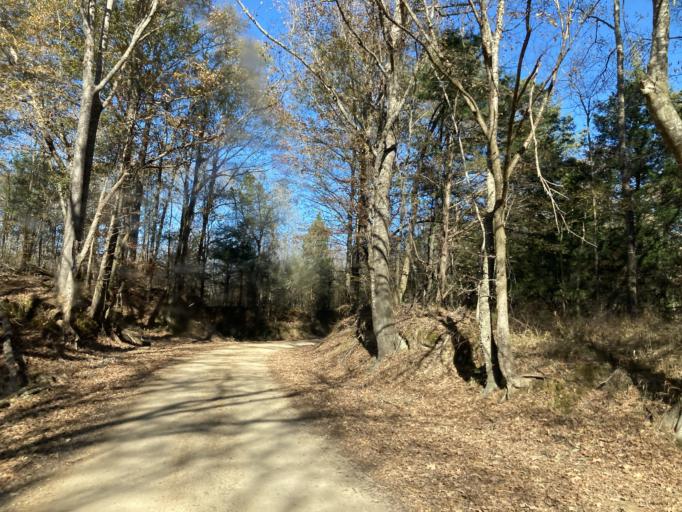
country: US
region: Mississippi
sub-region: Madison County
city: Kearney Park
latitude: 32.6180
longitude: -90.4564
